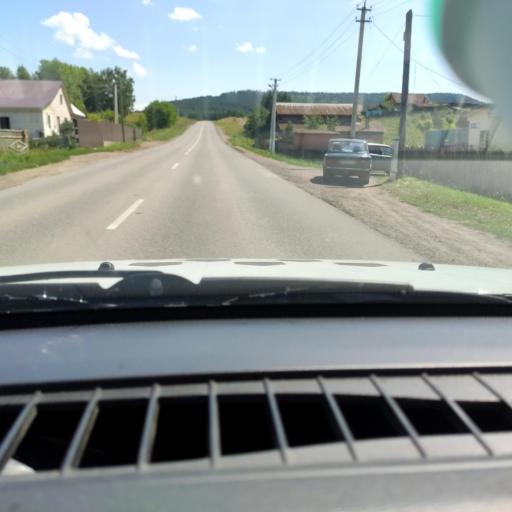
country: RU
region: Bashkortostan
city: Mesyagutovo
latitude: 55.5239
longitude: 58.2849
